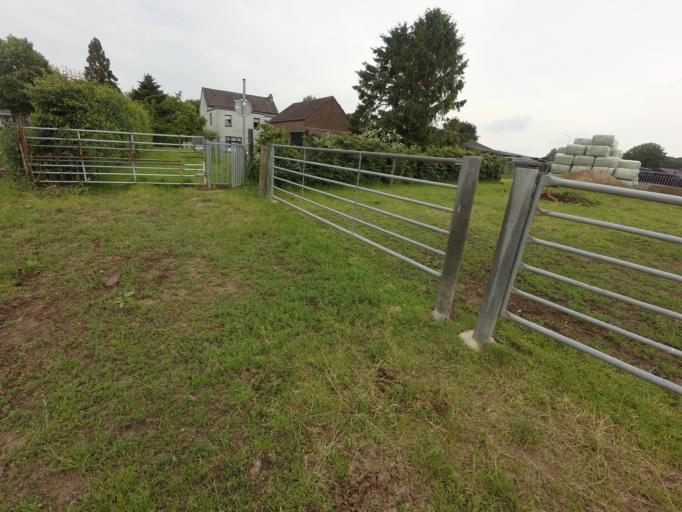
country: NL
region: Limburg
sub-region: Gemeente Simpelveld
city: Simpelveld
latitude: 50.8465
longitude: 5.9686
